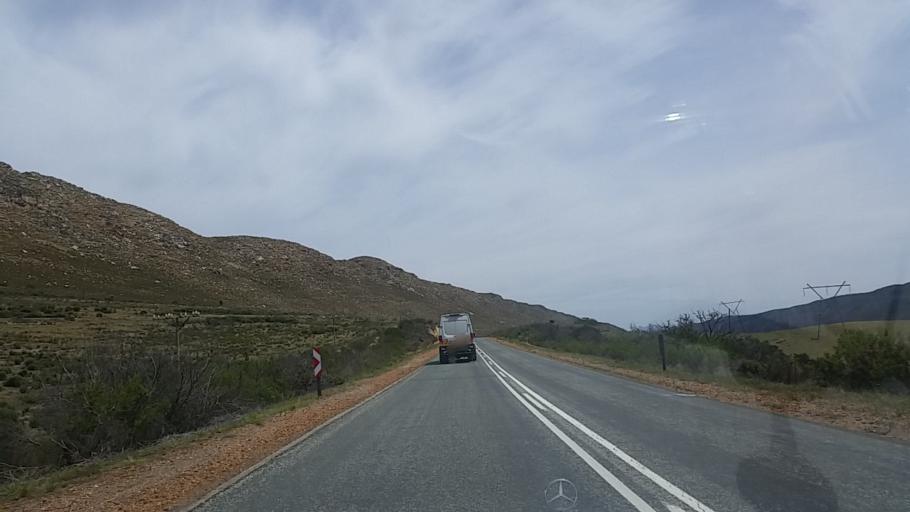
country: ZA
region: Western Cape
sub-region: Eden District Municipality
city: Knysna
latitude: -33.7406
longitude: 23.0364
